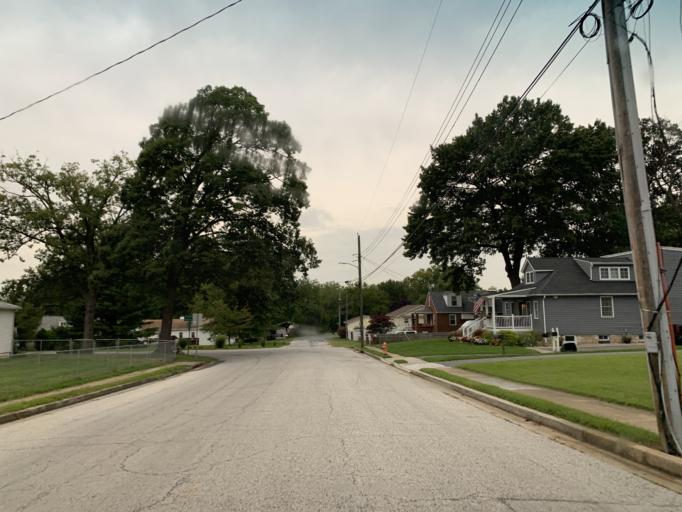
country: US
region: Maryland
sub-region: Baltimore County
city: Essex
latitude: 39.3174
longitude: -76.4816
